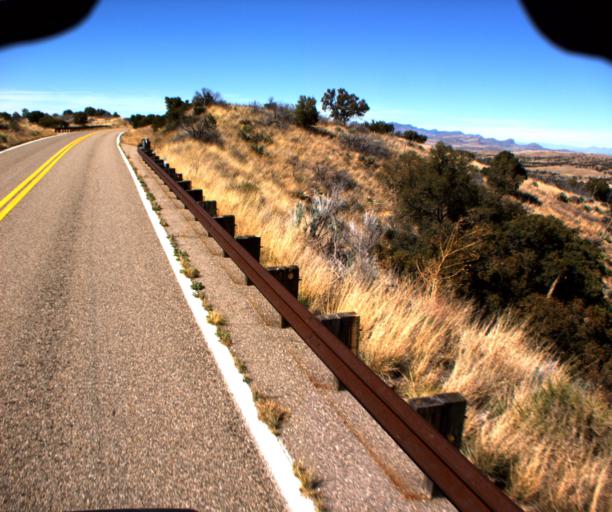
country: US
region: Arizona
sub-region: Cochise County
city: Sierra Vista
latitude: 31.5114
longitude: -110.4965
